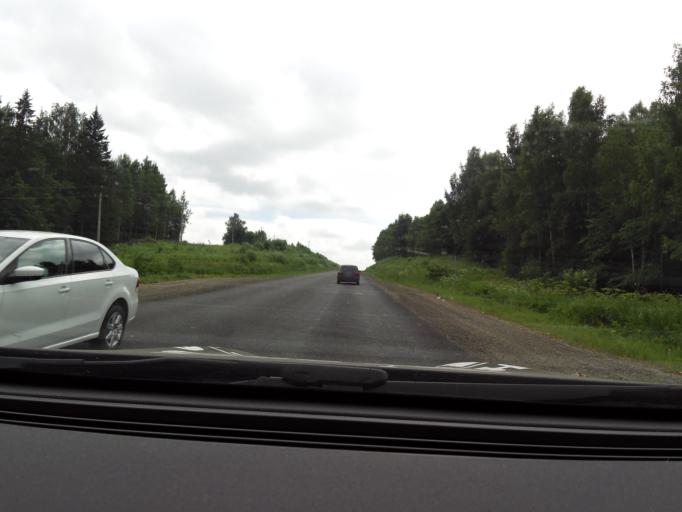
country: RU
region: Perm
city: Bershet'
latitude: 57.7548
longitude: 56.3658
